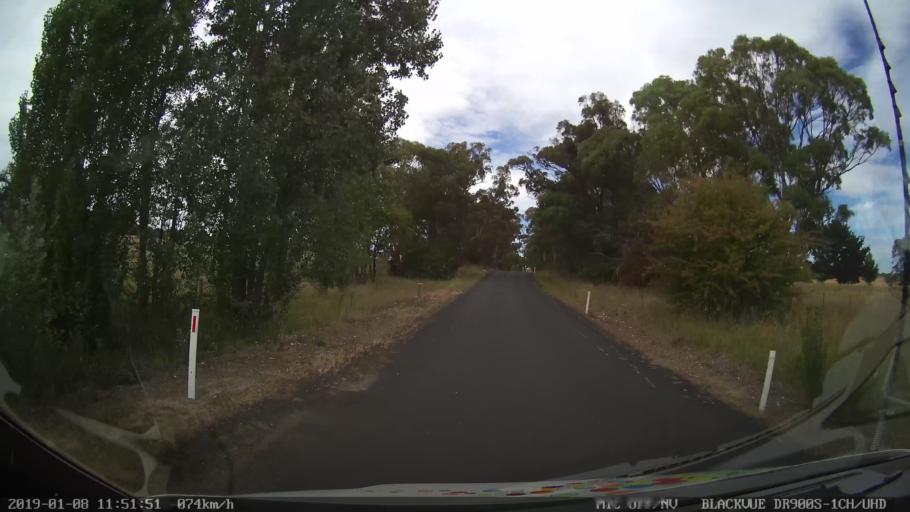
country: AU
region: New South Wales
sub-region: Armidale Dumaresq
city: Armidale
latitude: -30.3974
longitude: 151.5610
